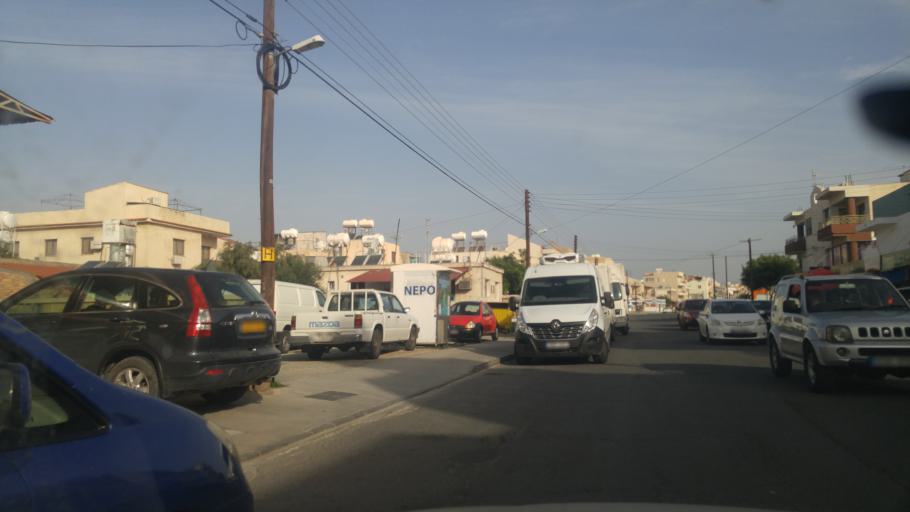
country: CY
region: Limassol
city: Limassol
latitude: 34.6661
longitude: 33.0039
